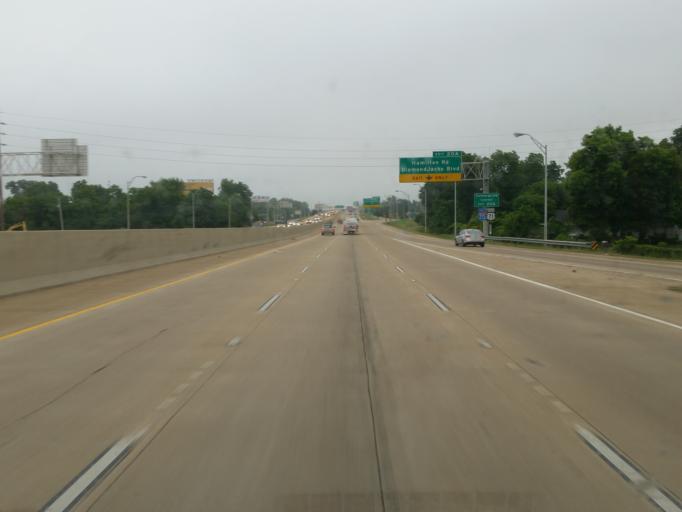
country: US
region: Louisiana
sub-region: Bossier Parish
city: Bossier City
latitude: 32.5139
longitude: -93.7320
